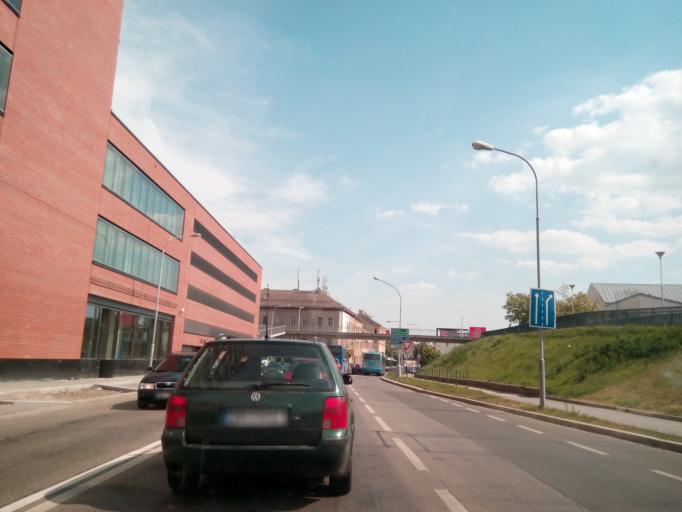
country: CZ
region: South Moravian
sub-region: Mesto Brno
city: Brno
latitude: 49.1876
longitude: 16.6167
